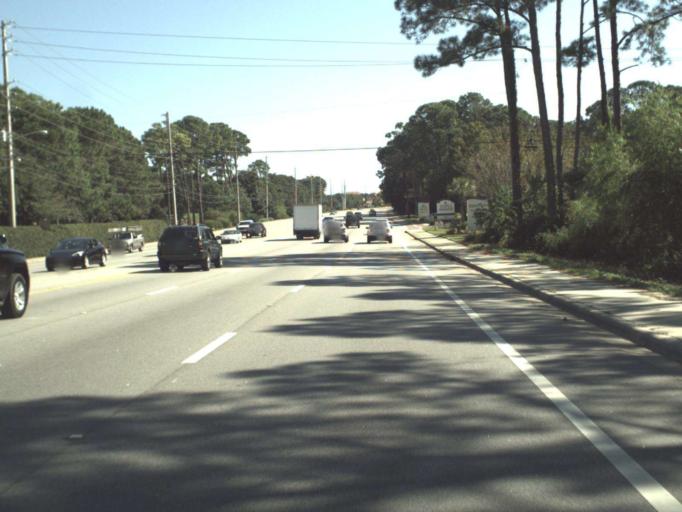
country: US
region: Florida
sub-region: Walton County
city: Miramar Beach
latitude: 30.3785
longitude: -86.3277
